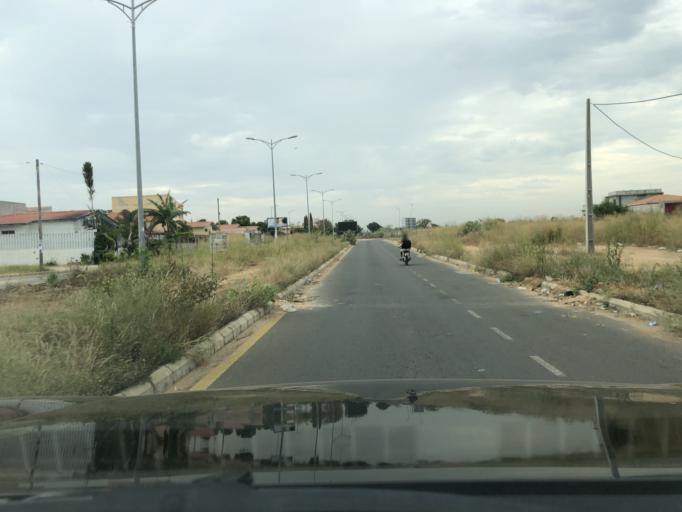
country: AO
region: Luanda
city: Luanda
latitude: -8.9457
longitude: 13.2525
